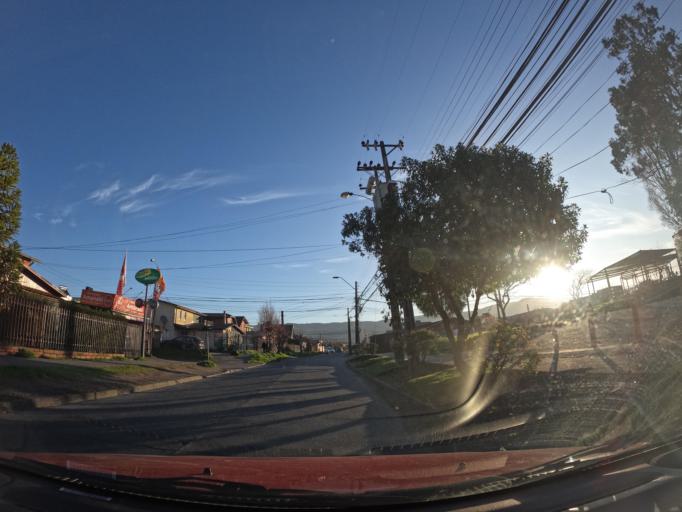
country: CL
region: Biobio
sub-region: Provincia de Concepcion
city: Chiguayante
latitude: -36.9210
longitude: -73.0299
